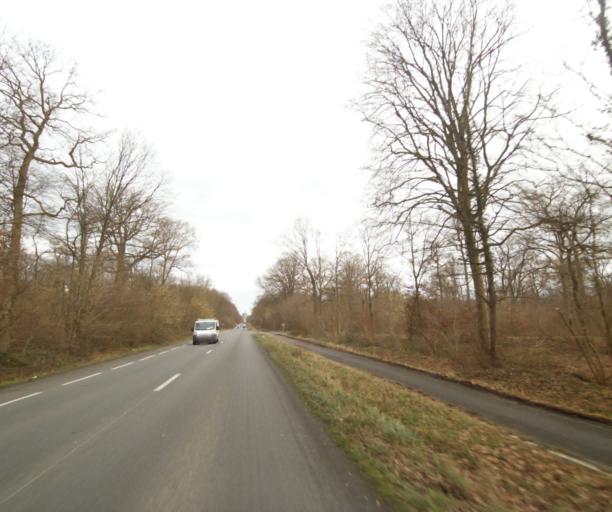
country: FR
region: Nord-Pas-de-Calais
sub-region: Departement du Nord
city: Conde-sur-l'Escaut
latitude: 50.4775
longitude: 3.5998
